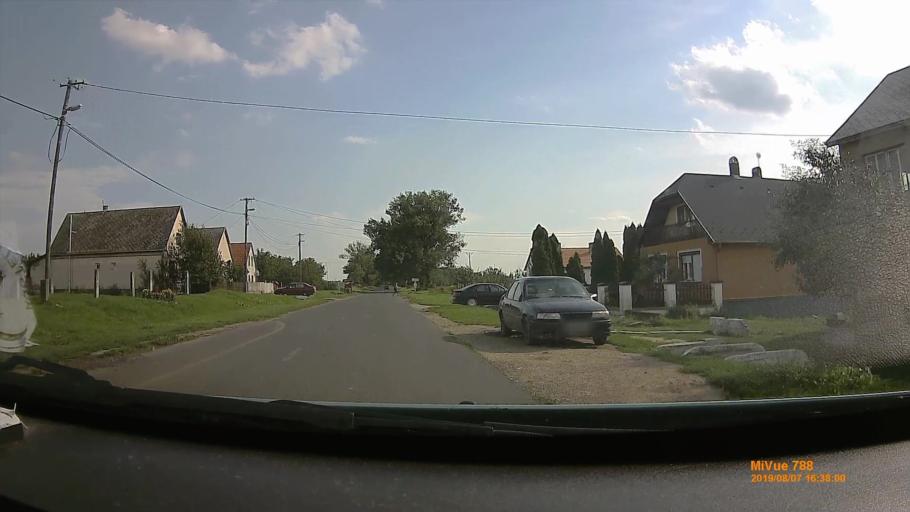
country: HU
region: Borsod-Abauj-Zemplen
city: Gonc
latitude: 48.4077
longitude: 21.2297
